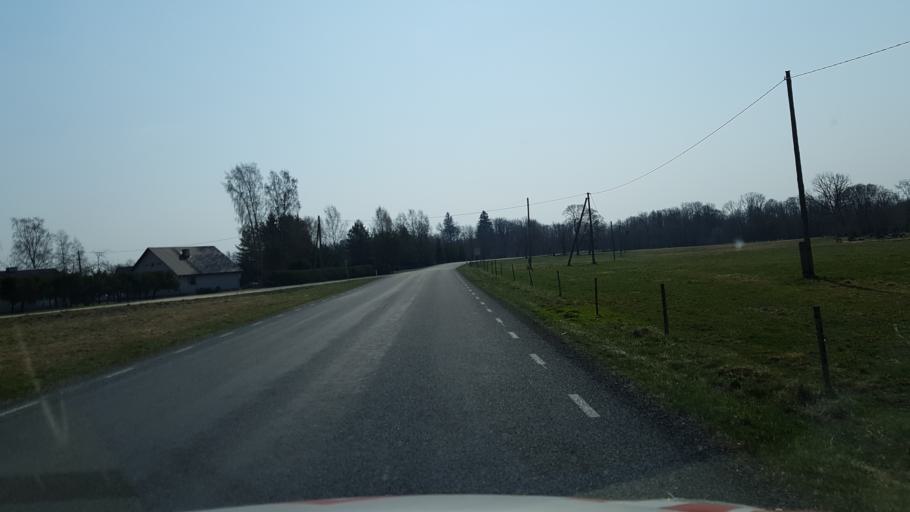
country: EE
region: Raplamaa
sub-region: Kehtna vald
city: Kehtna
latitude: 59.0273
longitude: 24.9248
